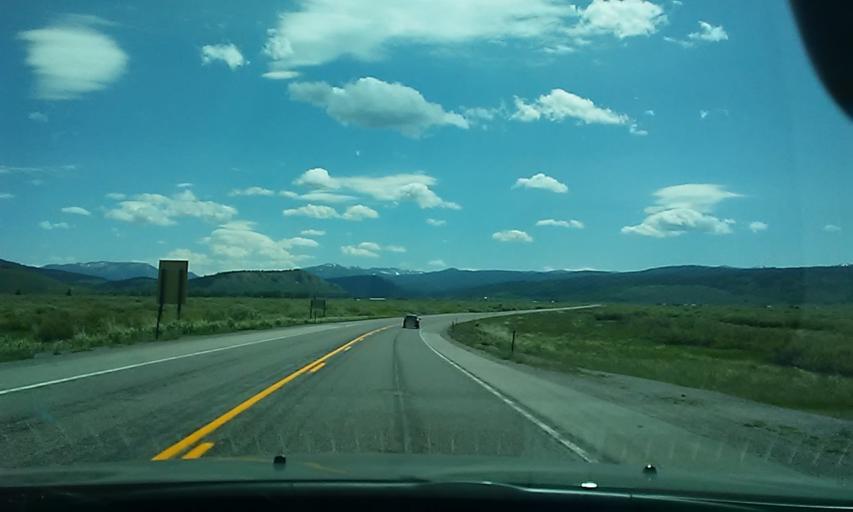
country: US
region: Wyoming
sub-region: Teton County
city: Jackson
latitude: 43.8381
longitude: -110.4396
